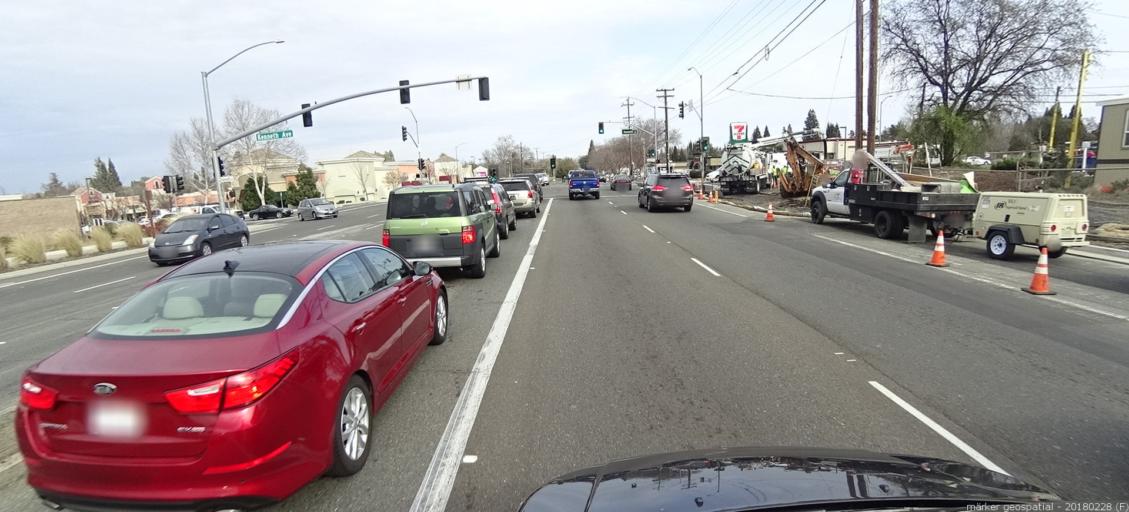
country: US
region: California
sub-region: Sacramento County
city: Orangevale
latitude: 38.6642
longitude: -121.2450
